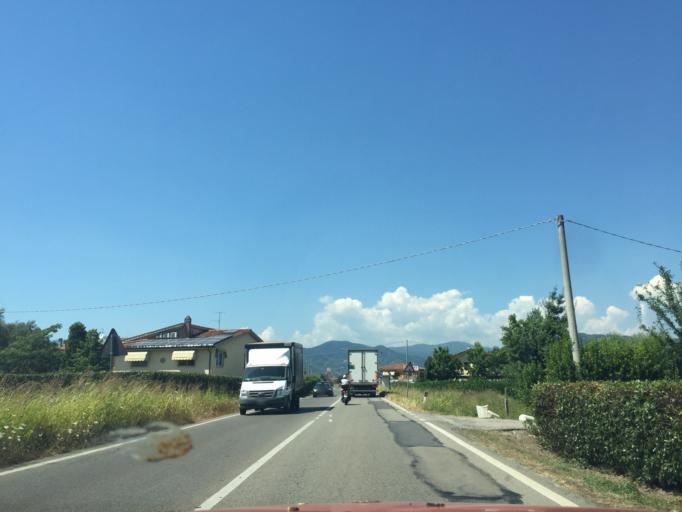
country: IT
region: Tuscany
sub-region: Provincia di Pistoia
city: Chiesina Uzzanese
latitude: 43.8484
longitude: 10.7106
